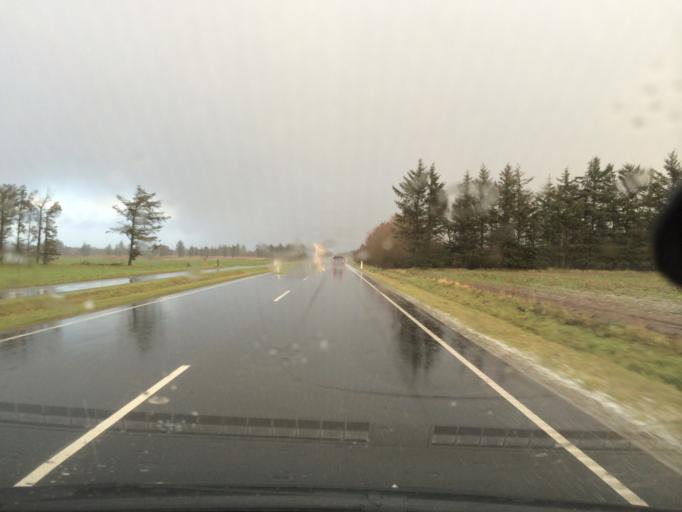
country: DK
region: Central Jutland
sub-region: Holstebro Kommune
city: Ulfborg
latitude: 56.2684
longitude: 8.2741
